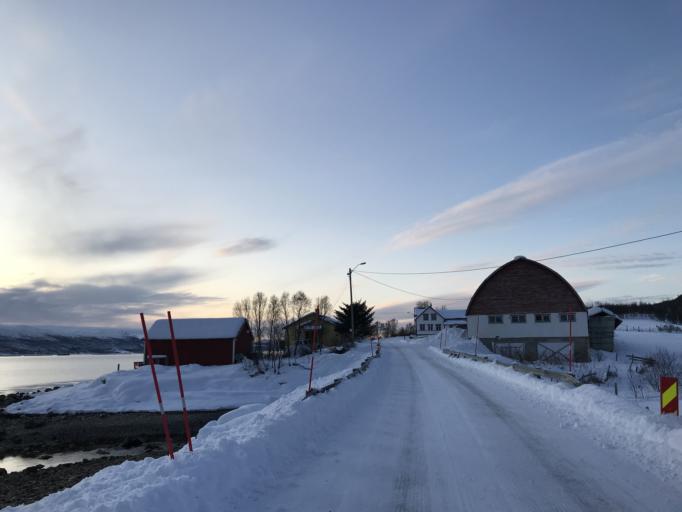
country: NO
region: Troms
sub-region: Karlsoy
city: Hansnes
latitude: 69.8477
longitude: 19.5423
